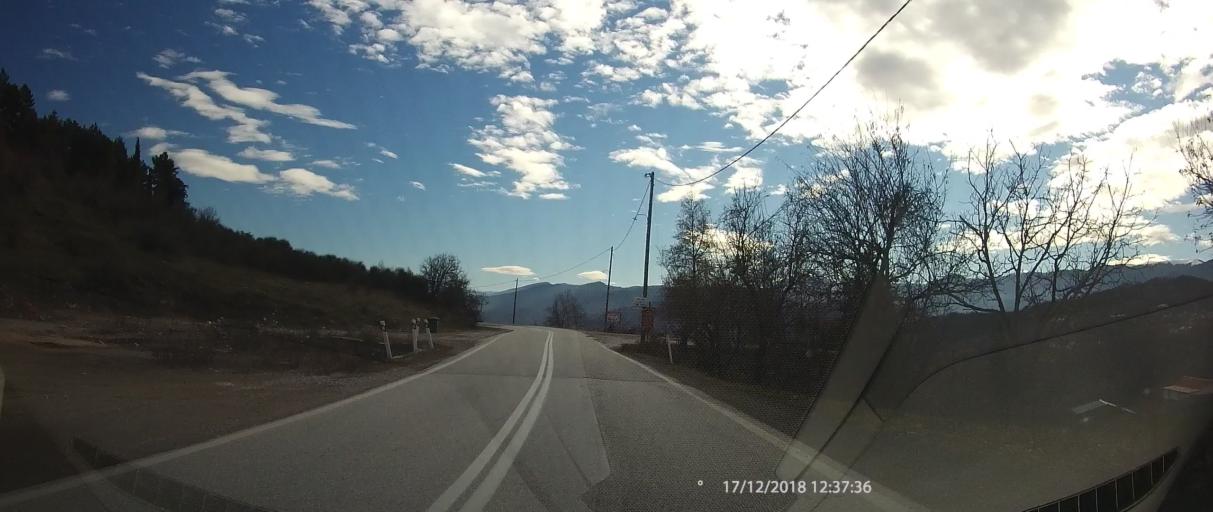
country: GR
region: Epirus
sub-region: Nomos Ioanninon
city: Metsovo
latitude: 39.8099
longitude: 21.3385
